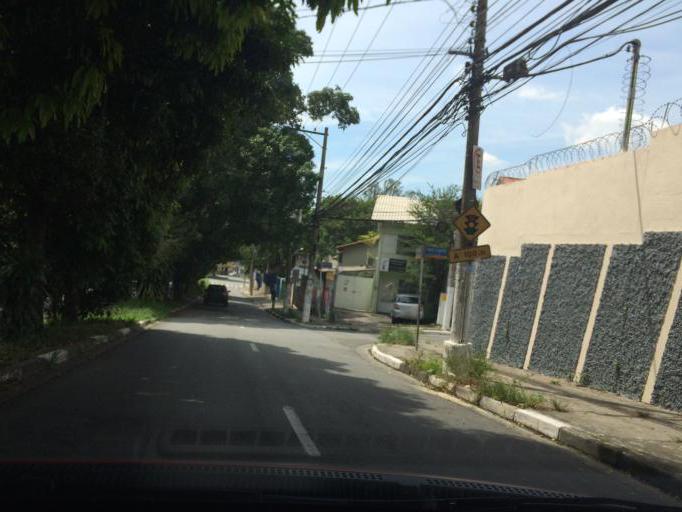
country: BR
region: Sao Paulo
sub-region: Osasco
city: Osasco
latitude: -23.5485
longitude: -46.7447
